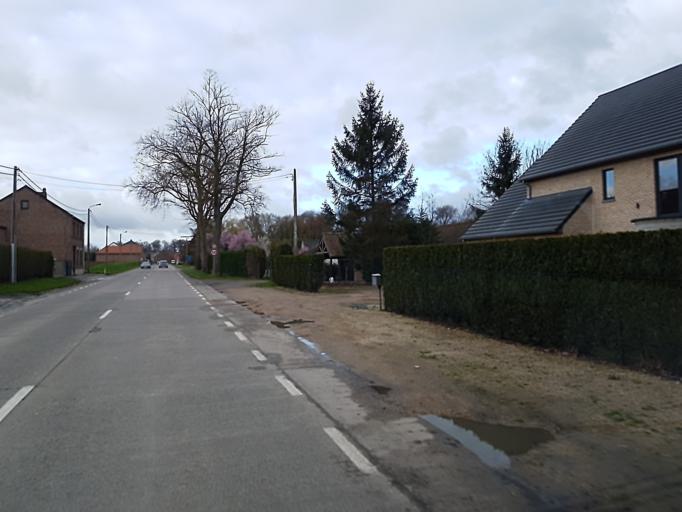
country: BE
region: Flanders
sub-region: Provincie Vlaams-Brabant
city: Hoegaarden
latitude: 50.7652
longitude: 4.9047
